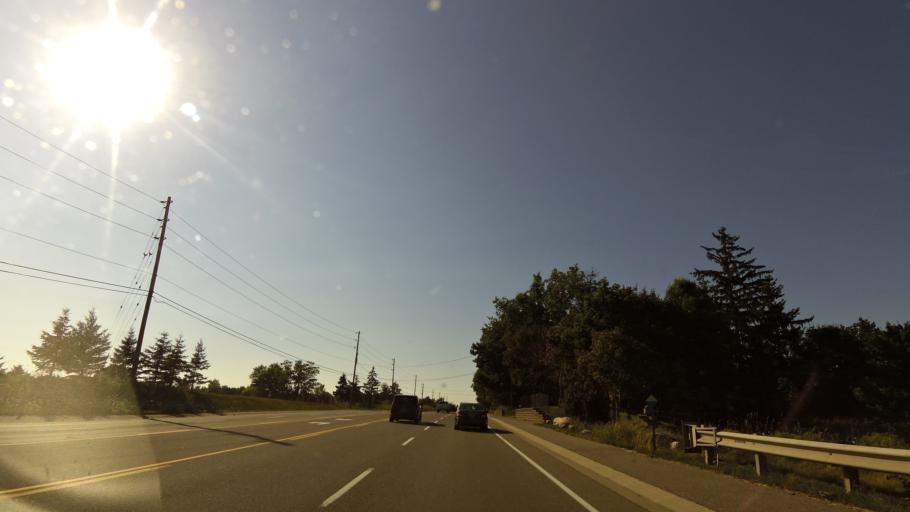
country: CA
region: Ontario
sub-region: Halton
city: Milton
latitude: 43.5410
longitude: -79.7886
